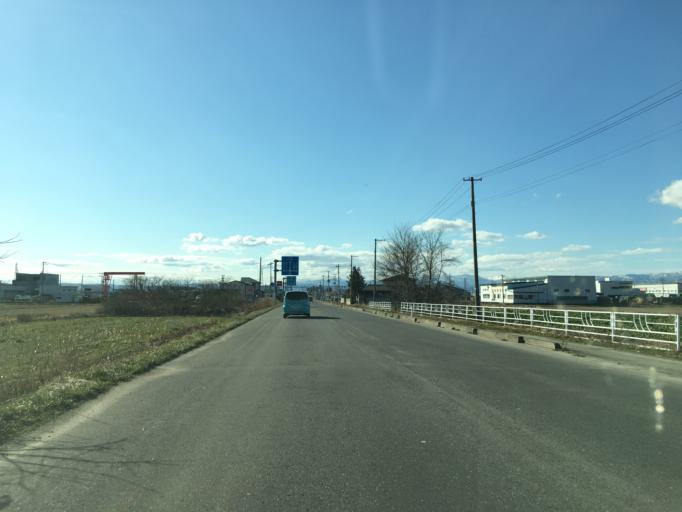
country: JP
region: Yamagata
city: Takahata
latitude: 38.0058
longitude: 140.1507
